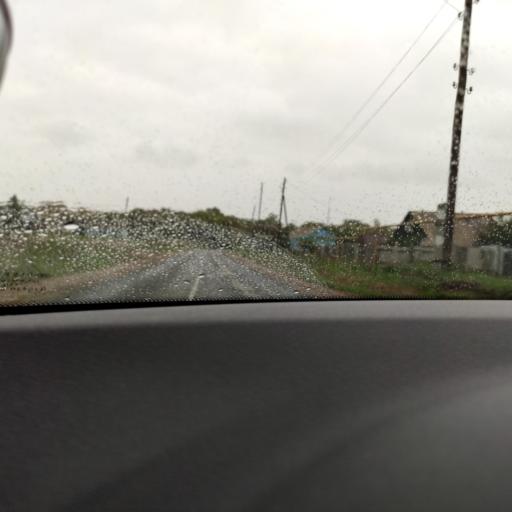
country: RU
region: Samara
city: Yelkhovka
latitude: 53.7435
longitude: 50.2621
